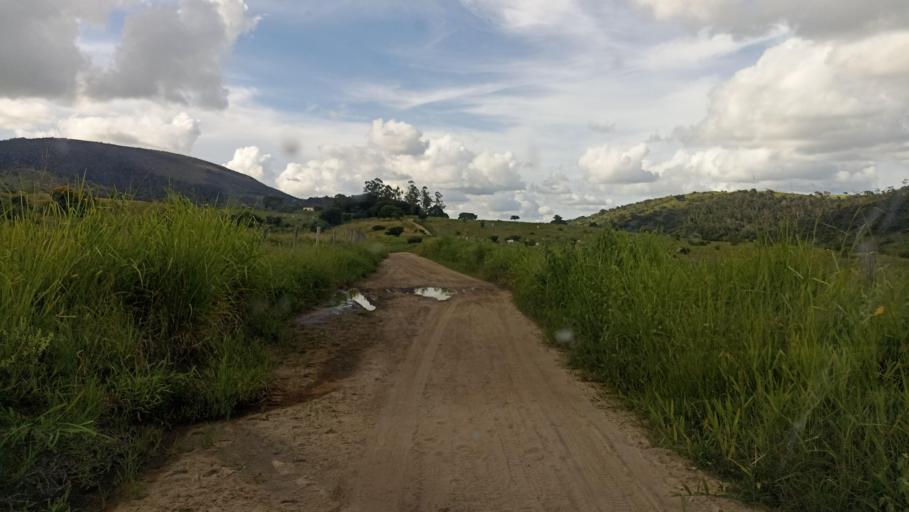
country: BR
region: Minas Gerais
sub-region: Almenara
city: Almenara
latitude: -16.6167
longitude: -40.4658
